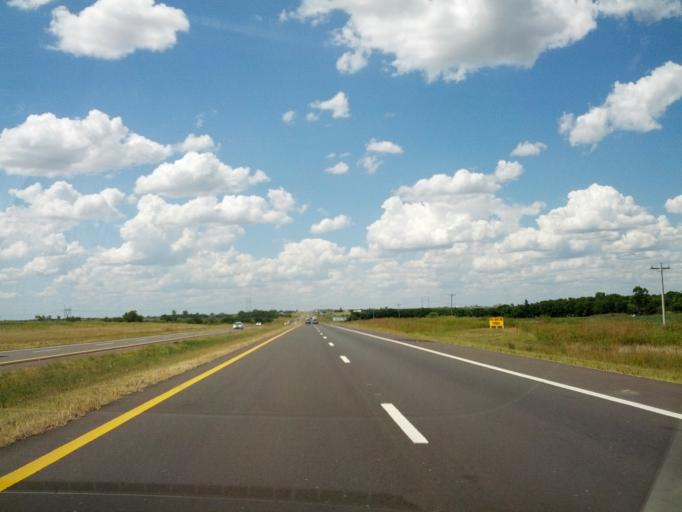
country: AR
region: Entre Rios
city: Colonia Elia
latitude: -32.5753
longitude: -58.3845
